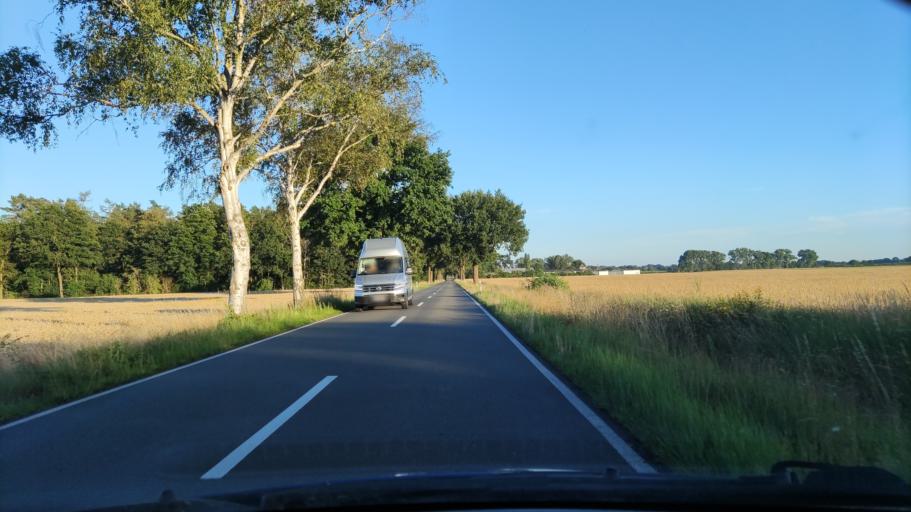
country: DE
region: Lower Saxony
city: Luechow
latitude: 53.0210
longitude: 11.1453
